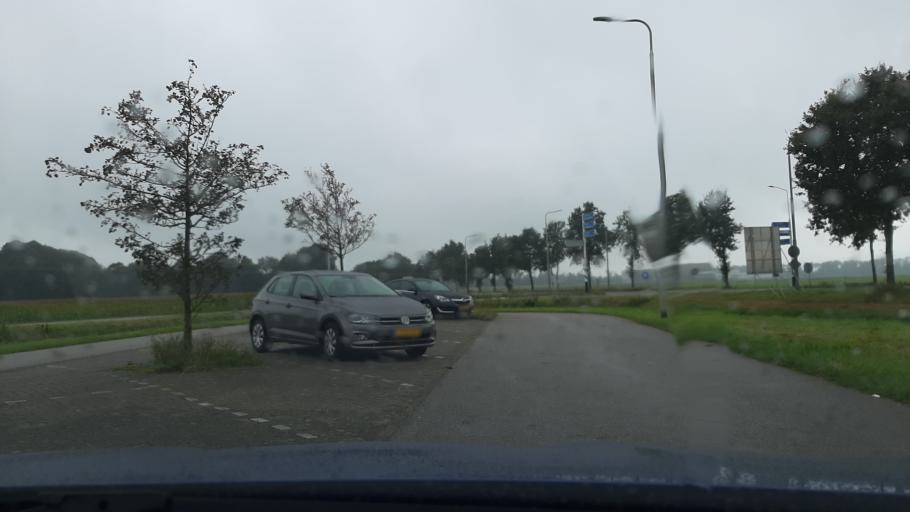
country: NL
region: Groningen
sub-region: Gemeente  Oldambt
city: Winschoten
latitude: 53.1830
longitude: 6.9720
